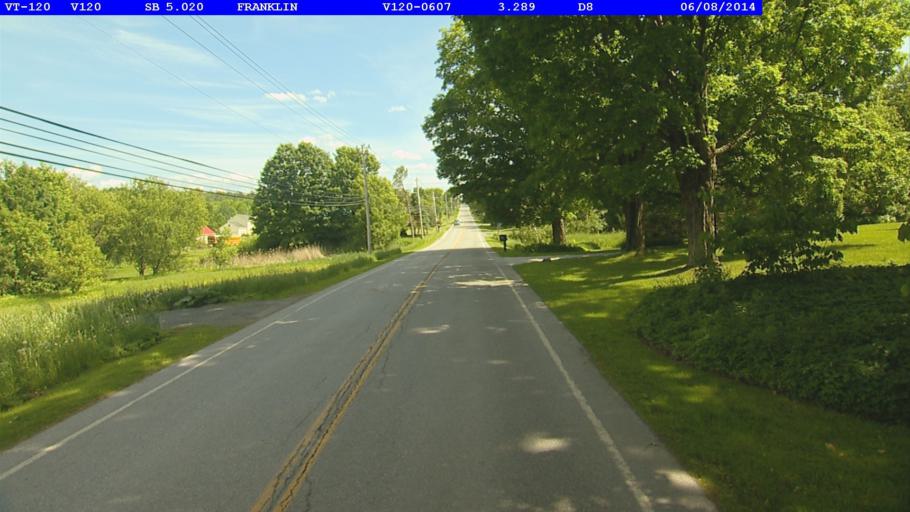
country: US
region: Vermont
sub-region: Franklin County
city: Enosburg Falls
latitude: 44.9794
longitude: -72.9145
